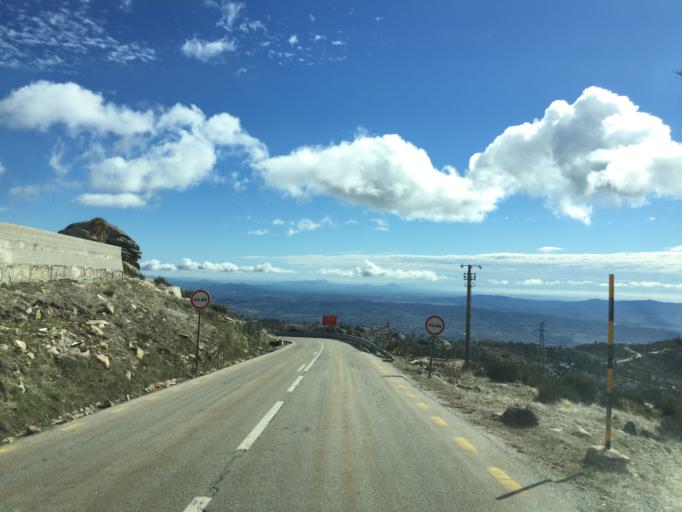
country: PT
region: Castelo Branco
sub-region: Covilha
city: Covilha
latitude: 40.3062
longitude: -7.5463
